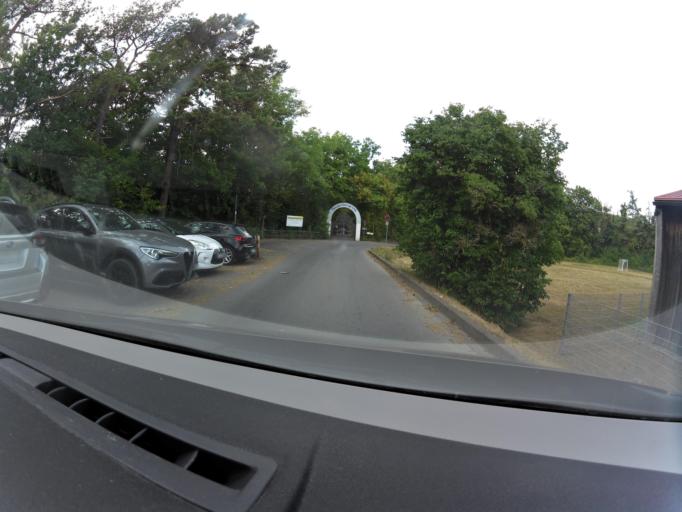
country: DE
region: Bavaria
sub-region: Regierungsbezirk Unterfranken
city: Bad Kissingen
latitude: 50.1913
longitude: 10.0873
